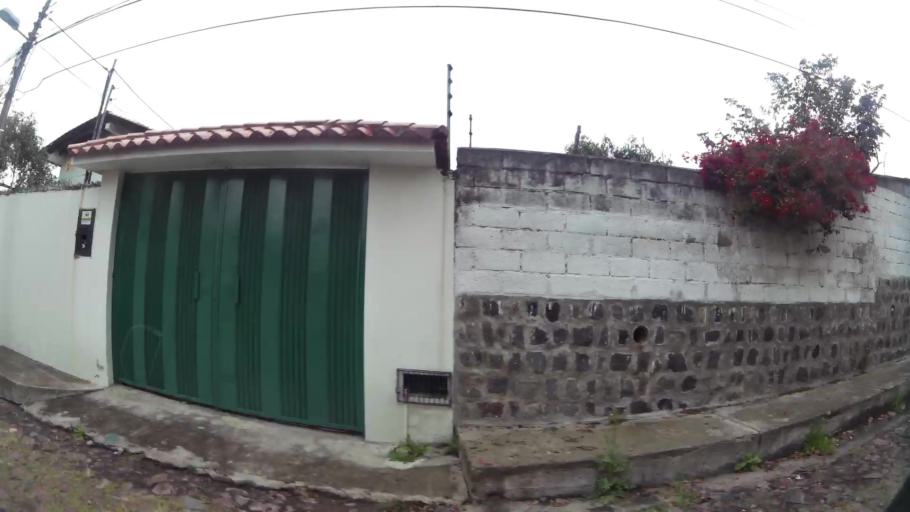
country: EC
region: Pichincha
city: Sangolqui
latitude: -0.2961
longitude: -78.4686
